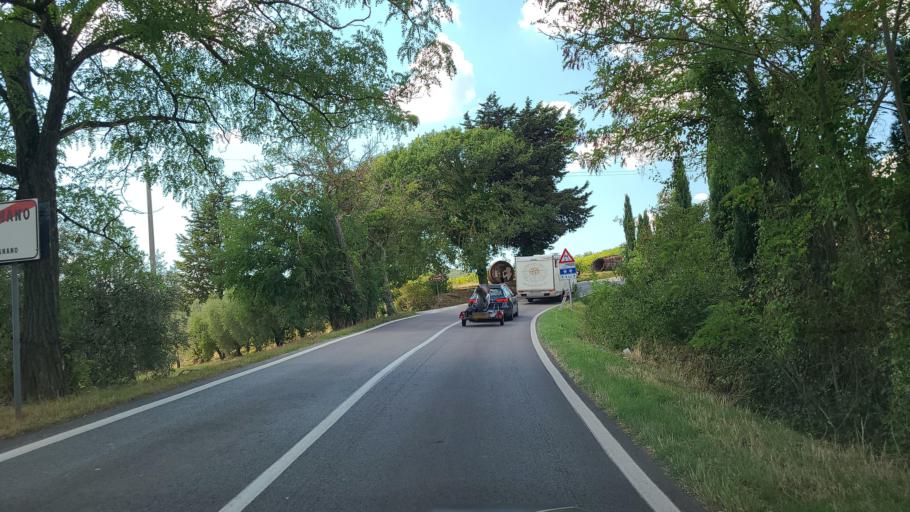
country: IT
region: Tuscany
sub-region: Provincia di Siena
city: Casole d'Elsa
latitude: 43.4035
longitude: 11.0155
